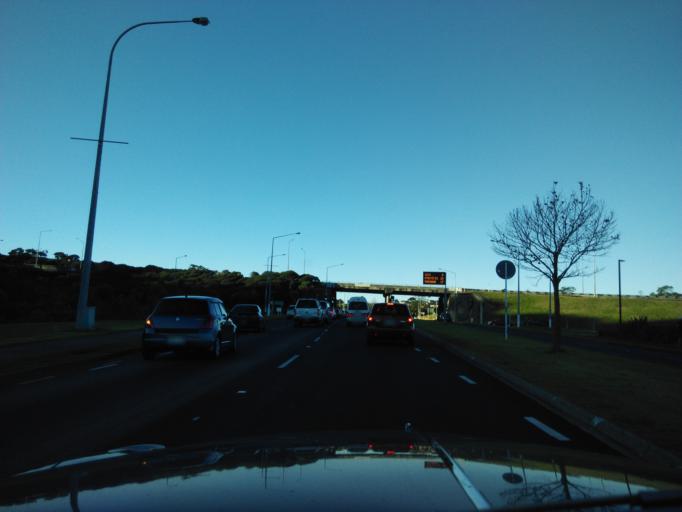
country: NZ
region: Auckland
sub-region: Auckland
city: Rothesay Bay
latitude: -36.7193
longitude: 174.7112
